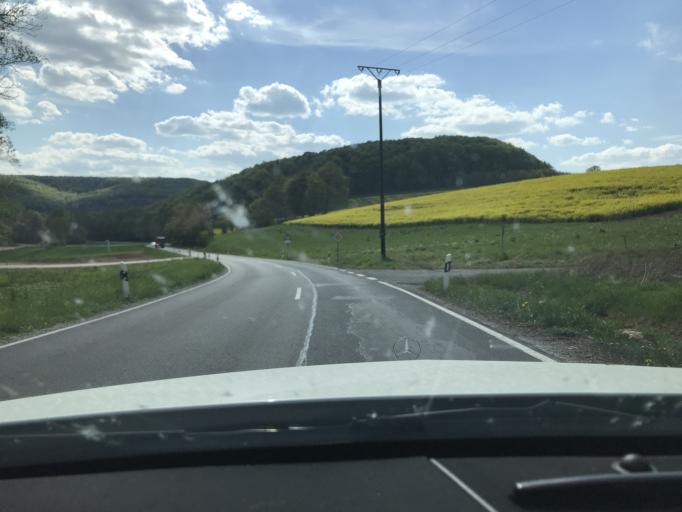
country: DE
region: Hesse
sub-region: Regierungsbezirk Kassel
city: Weissenborn
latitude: 51.1174
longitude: 10.0594
